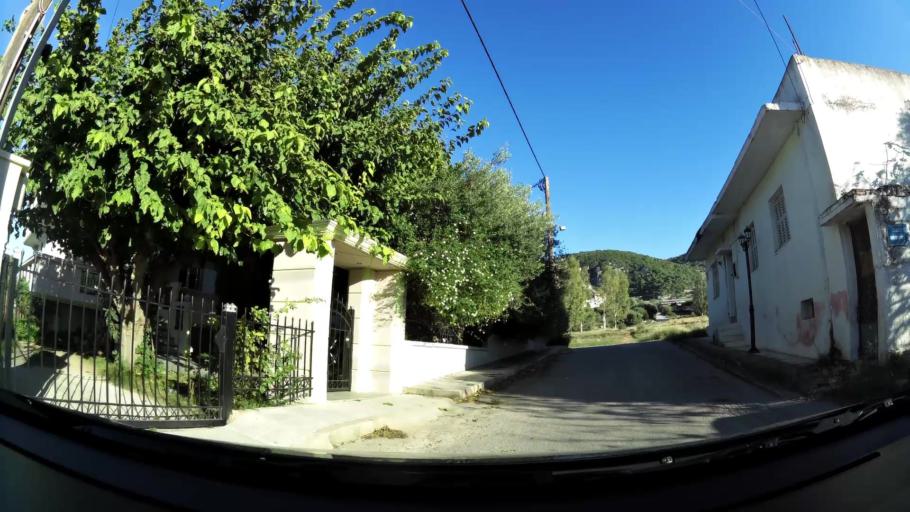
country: GR
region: Attica
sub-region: Nomarchia Athinas
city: Chaidari
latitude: 38.0365
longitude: 23.6342
